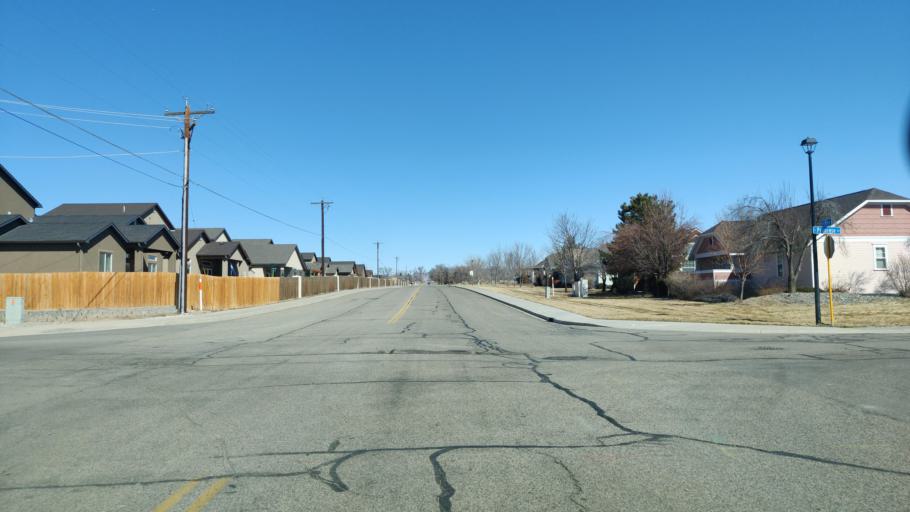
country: US
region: Colorado
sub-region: Mesa County
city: Fruita
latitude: 39.1733
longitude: -108.7197
